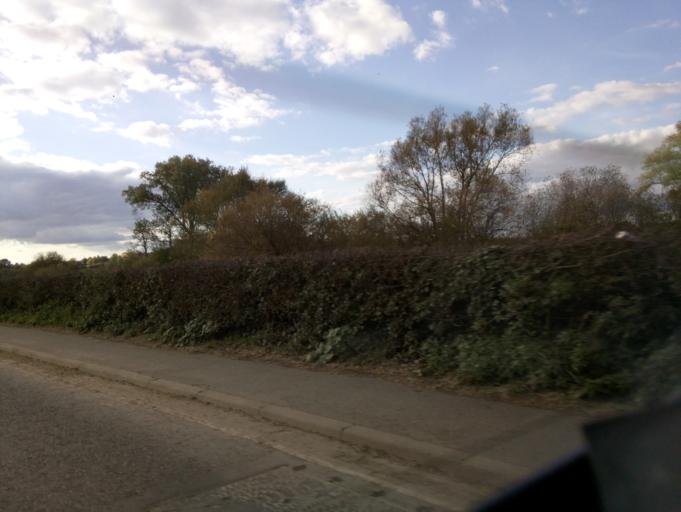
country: GB
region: England
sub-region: Herefordshire
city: Sutton
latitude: 52.0615
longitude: -2.6679
